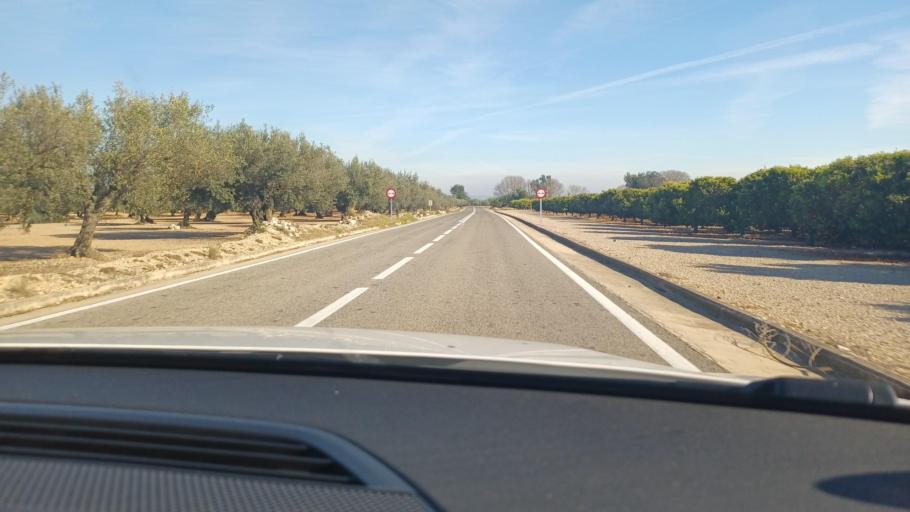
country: ES
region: Catalonia
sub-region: Provincia de Tarragona
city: Santa Barbara
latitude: 40.7214
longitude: 0.4343
